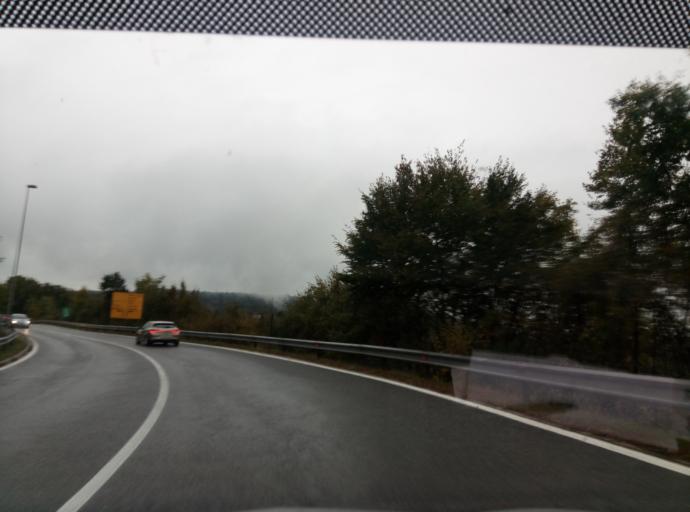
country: SI
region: Medvode
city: Zgornje Pirnice
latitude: 46.1061
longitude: 14.4685
